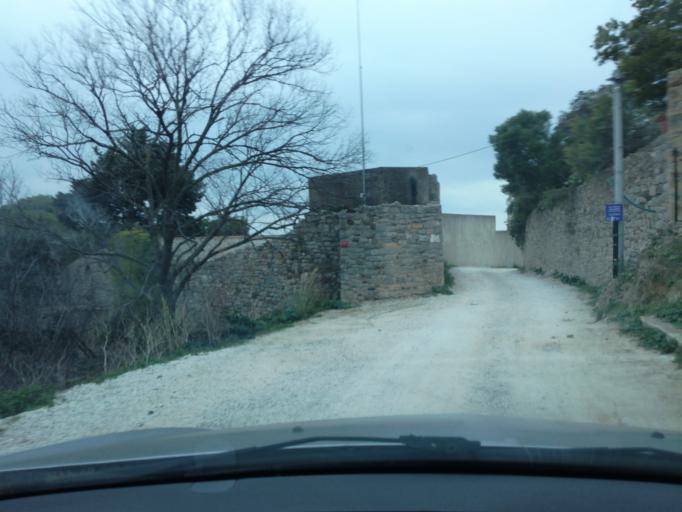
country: FR
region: Provence-Alpes-Cote d'Azur
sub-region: Departement du Var
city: Hyeres
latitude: 43.1246
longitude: 6.1263
